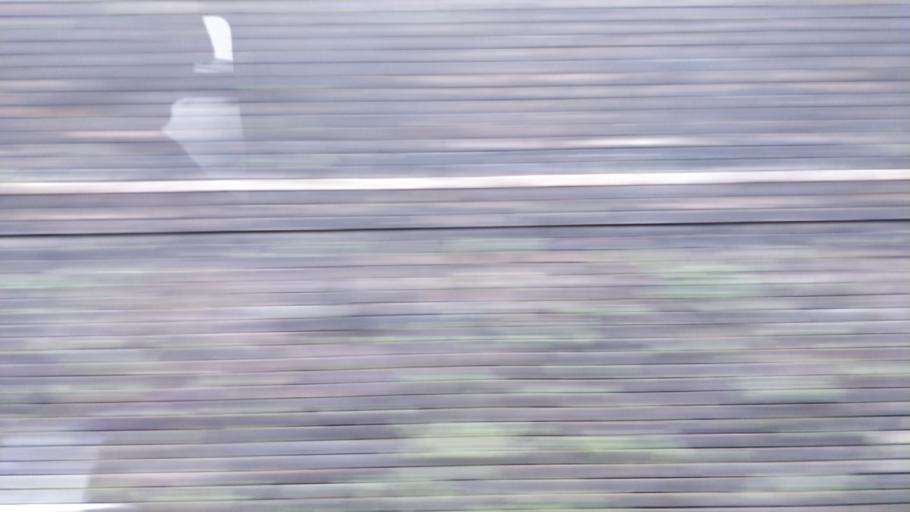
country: GB
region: England
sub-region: City and Borough of Salford
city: Salford
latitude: 53.4822
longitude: -2.2715
